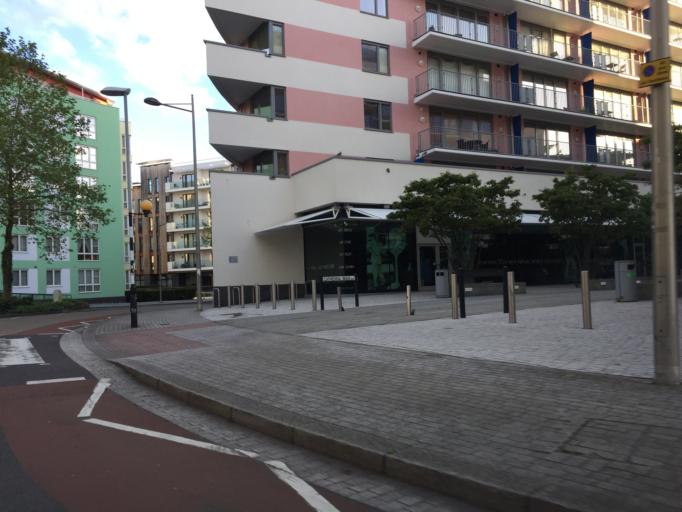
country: GB
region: England
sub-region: Bristol
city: Bristol
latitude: 51.4493
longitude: -2.6030
